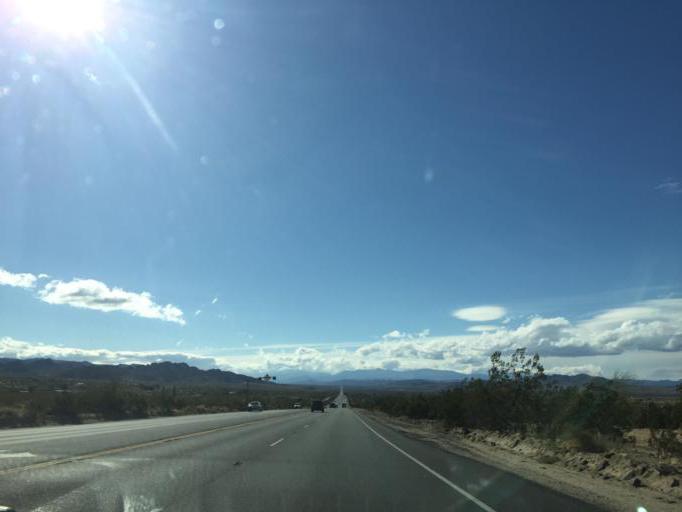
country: US
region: California
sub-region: San Bernardino County
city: Joshua Tree
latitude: 34.1352
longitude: -116.2127
